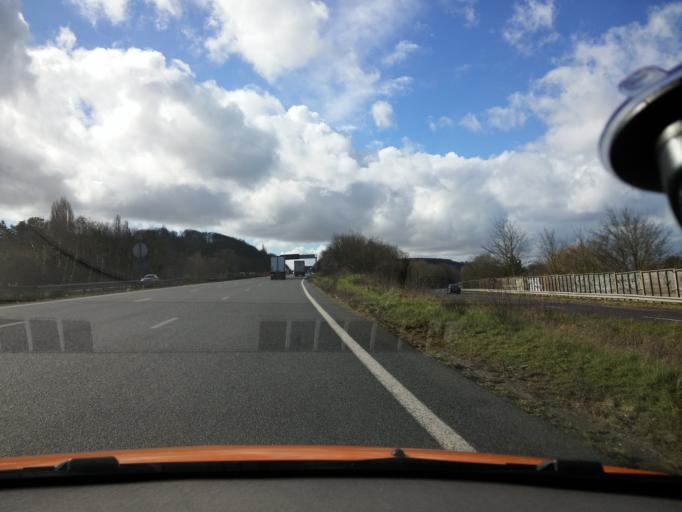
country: FR
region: Ile-de-France
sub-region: Departement de l'Essonne
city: Villebon-sur-Yvette
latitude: 48.6988
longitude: 2.2431
